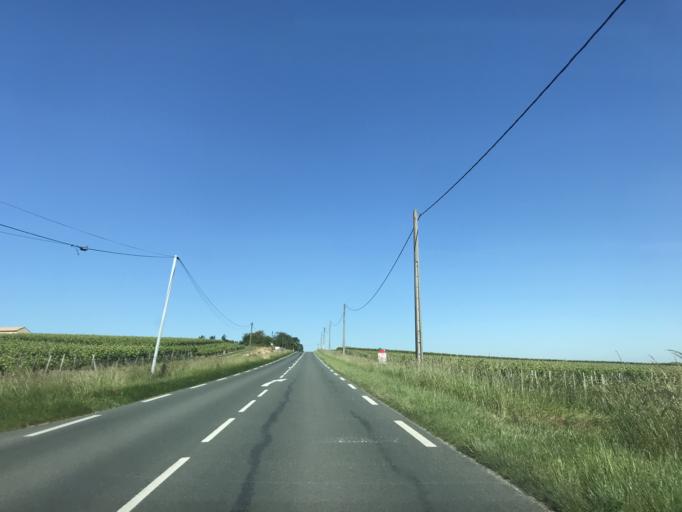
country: FR
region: Poitou-Charentes
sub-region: Departement de la Charente
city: Chateaubernard
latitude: 45.5400
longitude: -0.3416
